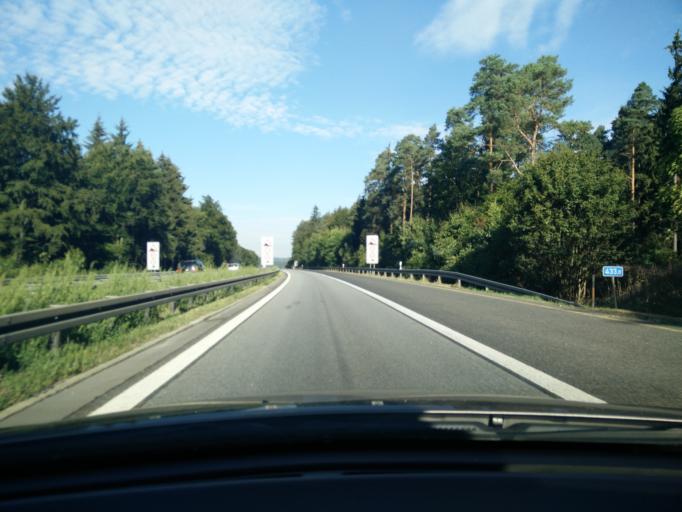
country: DE
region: Bavaria
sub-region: Upper Bavaria
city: Denkendorf
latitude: 48.9762
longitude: 11.4019
